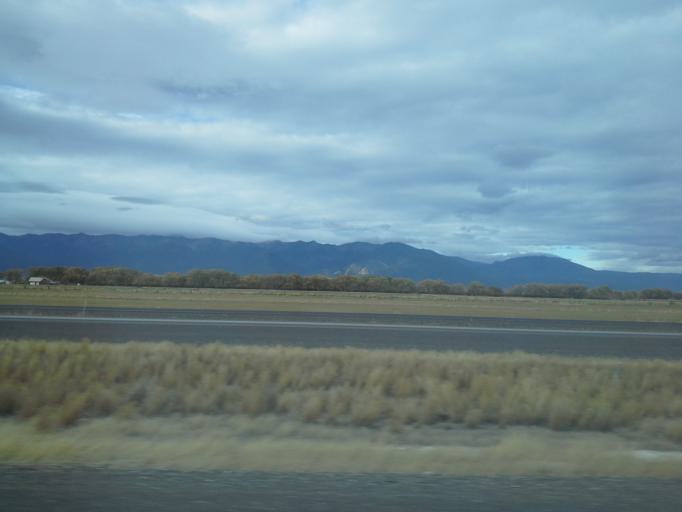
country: US
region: Oregon
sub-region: Baker County
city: Baker City
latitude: 44.8495
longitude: -117.8162
